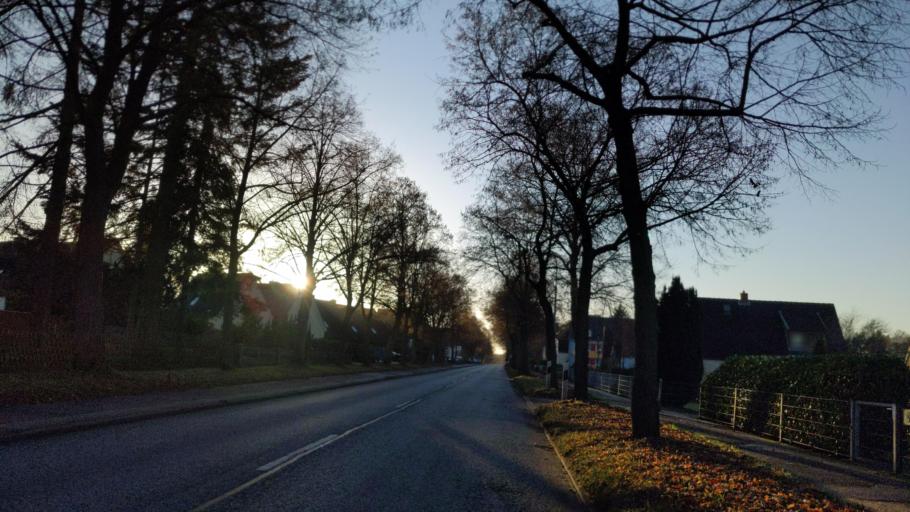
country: DE
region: Mecklenburg-Vorpommern
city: Selmsdorf
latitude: 53.8830
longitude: 10.7838
